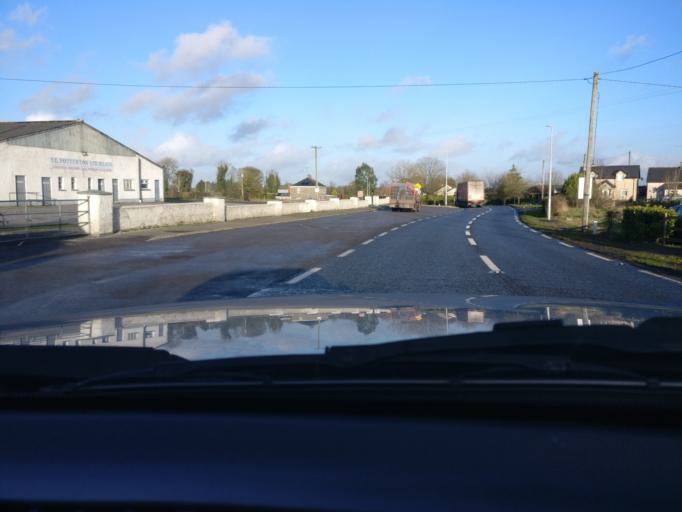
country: IE
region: Leinster
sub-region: An Iarmhi
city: Rathwire
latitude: 53.6160
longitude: -7.0887
